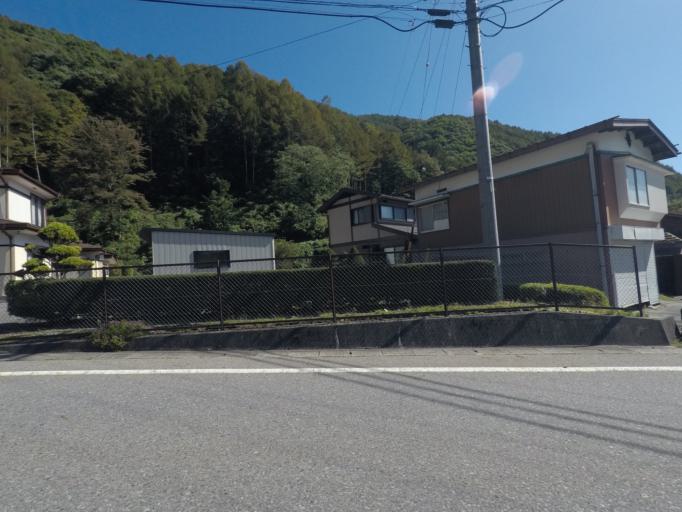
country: JP
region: Nagano
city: Shiojiri
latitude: 35.9853
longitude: 137.7424
